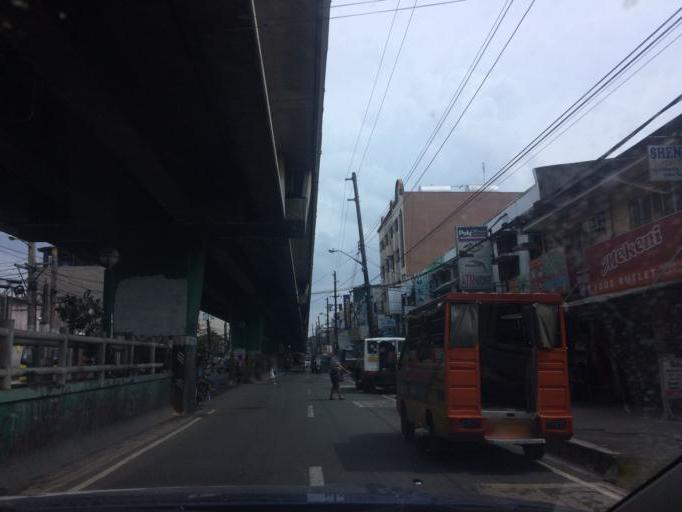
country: PH
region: Metro Manila
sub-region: Makati City
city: Makati City
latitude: 14.5517
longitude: 120.9977
